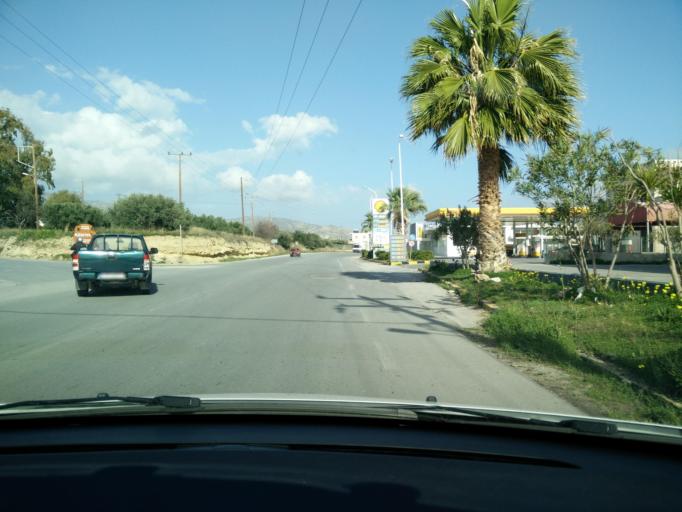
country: GR
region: Crete
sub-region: Nomos Lasithiou
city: Ierapetra
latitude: 35.0226
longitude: 25.7508
